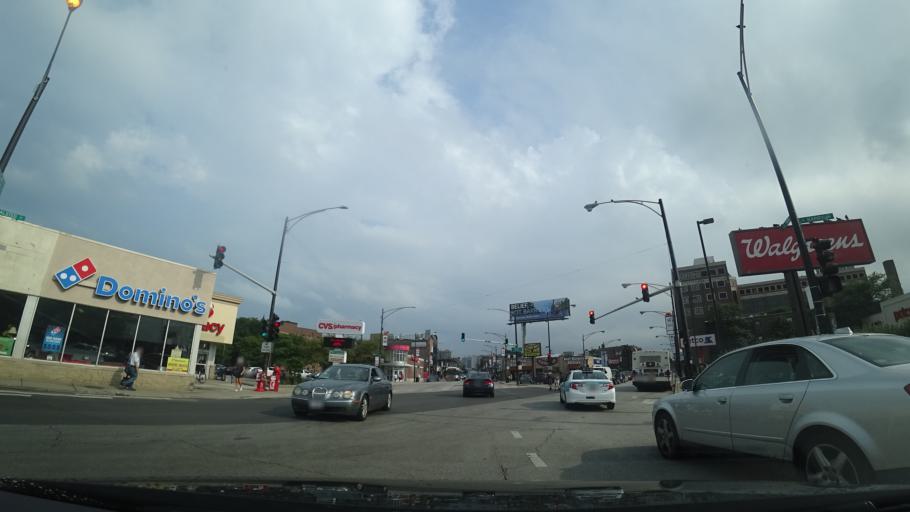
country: US
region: Illinois
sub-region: Cook County
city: Chicago
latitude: 41.9383
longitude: -87.6493
